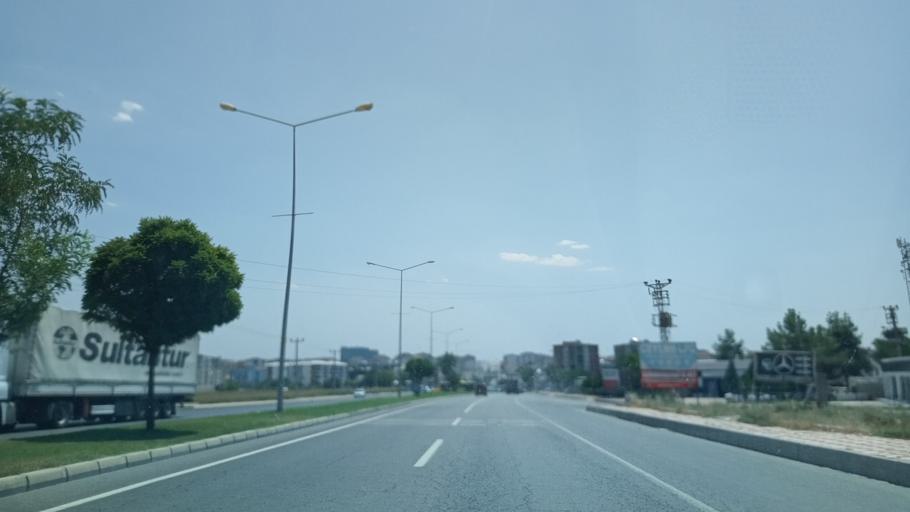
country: TR
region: Batman
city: Demiryol
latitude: 37.9268
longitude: 41.1365
